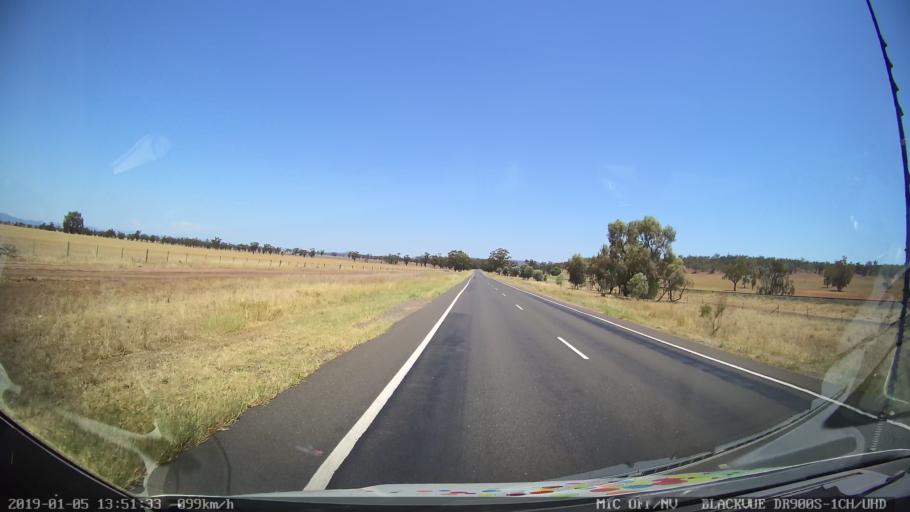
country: AU
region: New South Wales
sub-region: Gunnedah
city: Gunnedah
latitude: -31.0463
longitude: 150.2770
